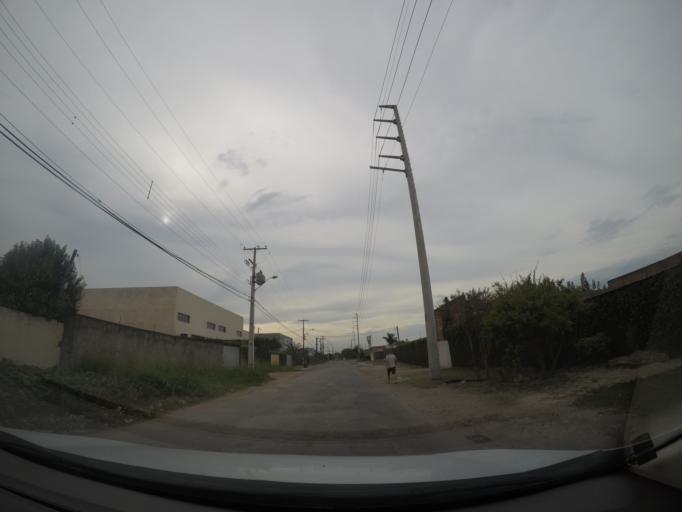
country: BR
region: Parana
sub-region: Sao Jose Dos Pinhais
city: Sao Jose dos Pinhais
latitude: -25.4934
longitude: -49.2304
